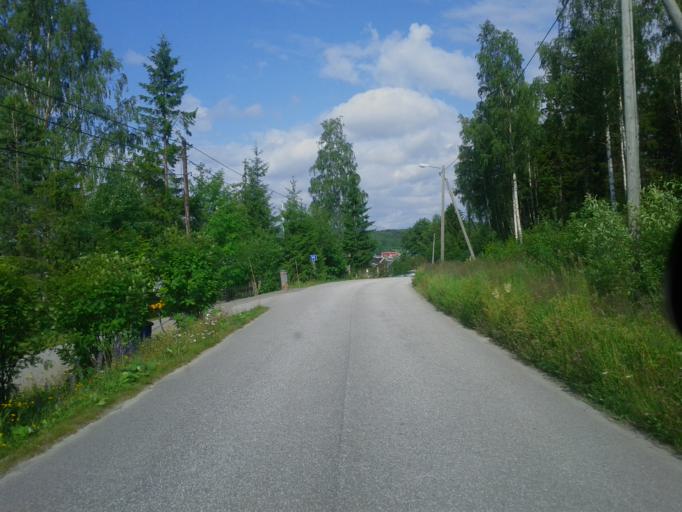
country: SE
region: Vaesternorrland
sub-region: OErnskoeldsviks Kommun
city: Ornskoldsvik
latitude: 63.2617
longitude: 18.8069
